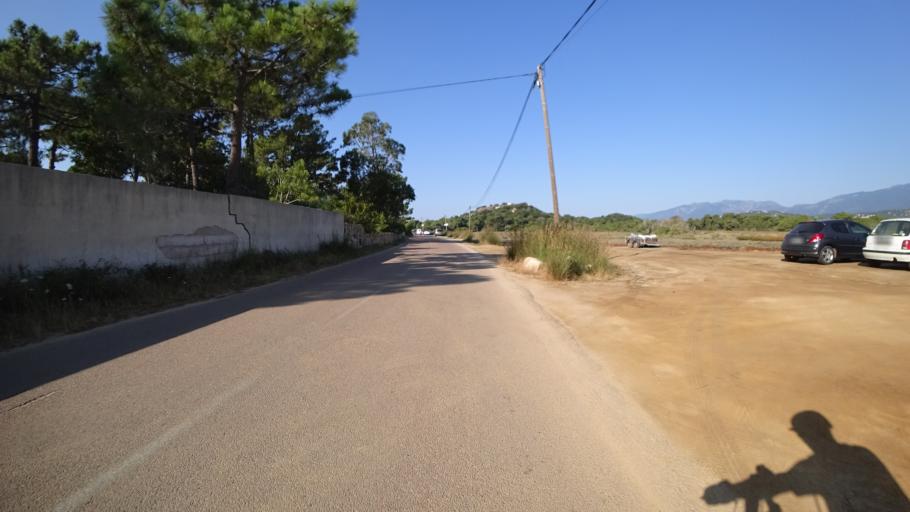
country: FR
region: Corsica
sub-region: Departement de la Corse-du-Sud
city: Porto-Vecchio
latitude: 41.6200
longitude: 9.3311
